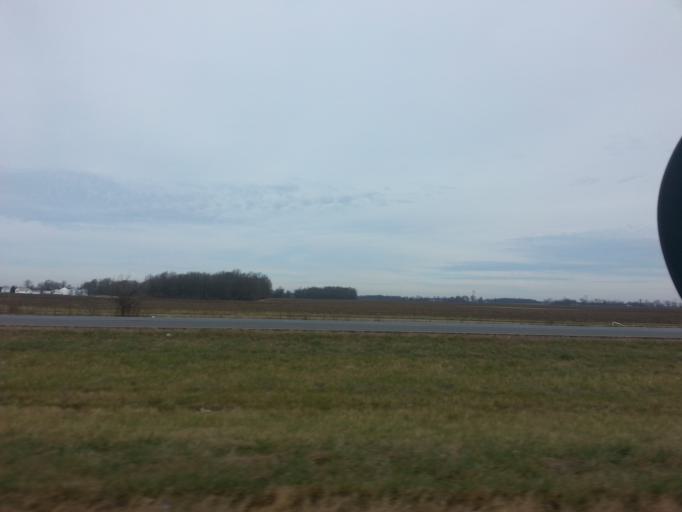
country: US
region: Indiana
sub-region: Hendricks County
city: Pittsboro
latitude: 39.8795
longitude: -86.4674
